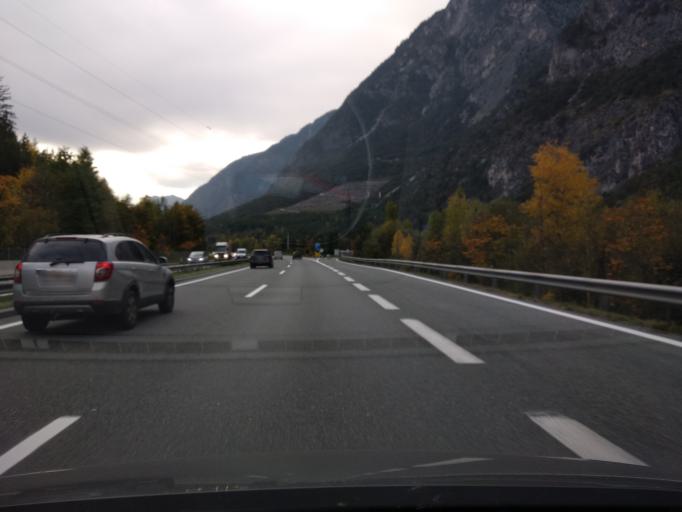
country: AT
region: Tyrol
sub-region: Politischer Bezirk Landeck
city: Schonwies
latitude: 47.1826
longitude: 10.6238
